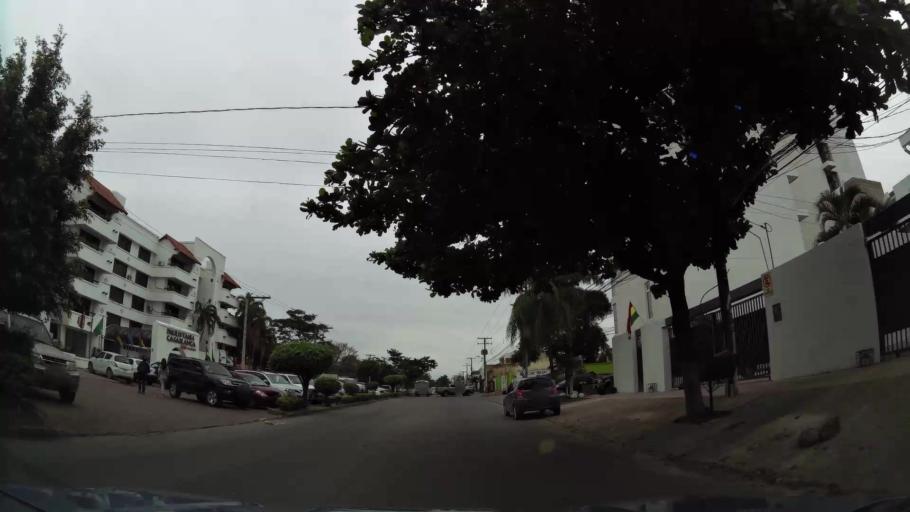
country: BO
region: Santa Cruz
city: Santa Cruz de la Sierra
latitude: -17.7617
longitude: -63.1942
